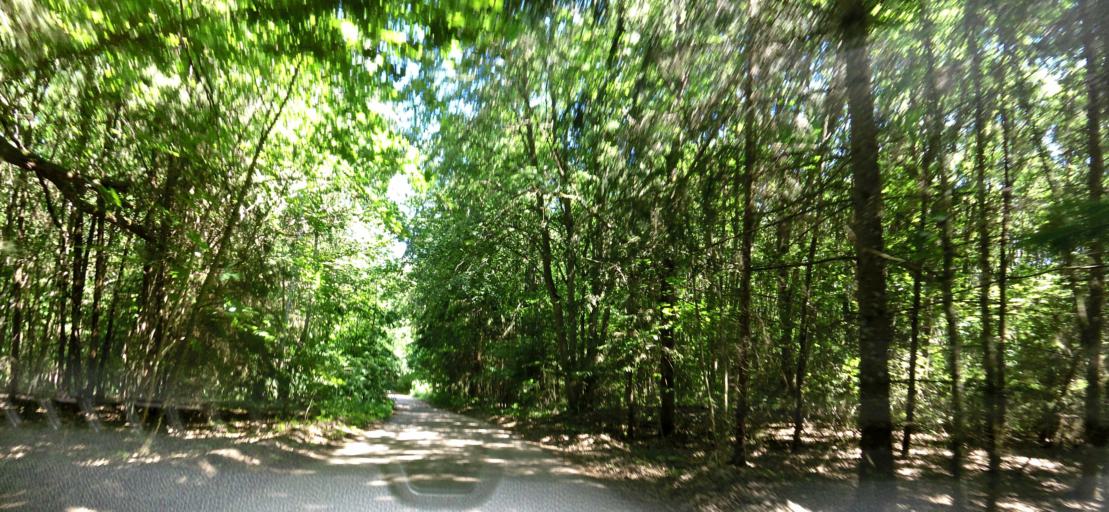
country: LT
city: Grigiskes
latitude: 54.8026
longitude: 24.9918
